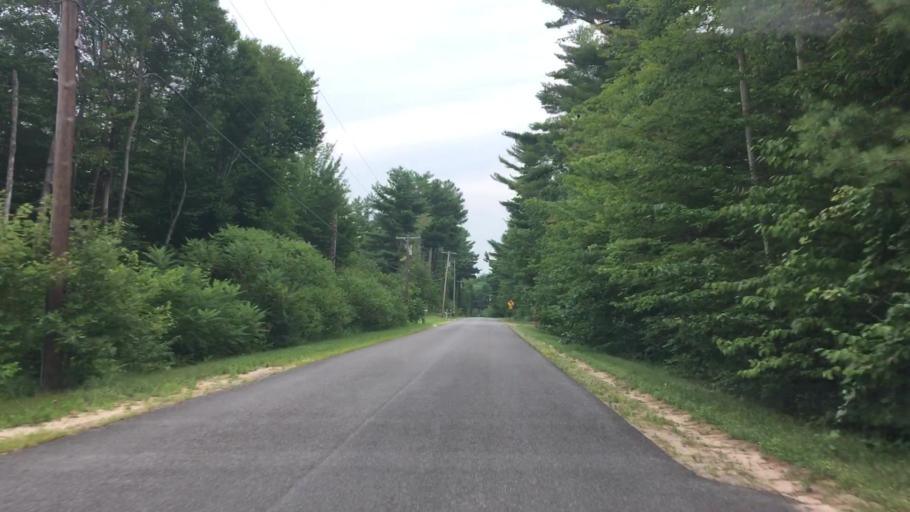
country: US
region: New York
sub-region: Clinton County
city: Peru
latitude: 44.6028
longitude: -73.5957
